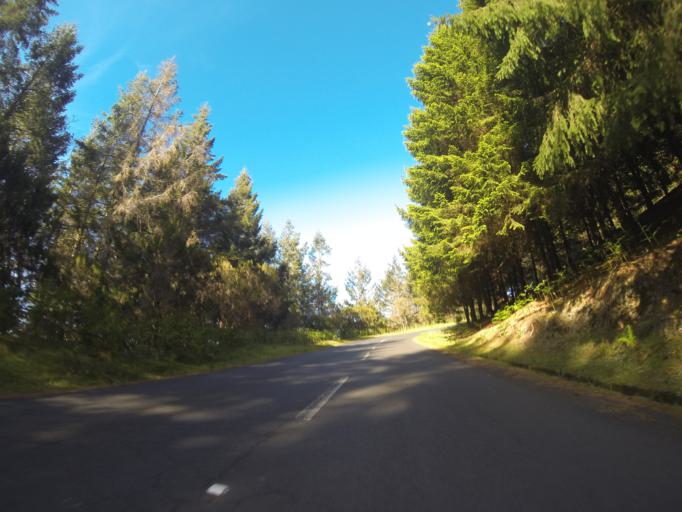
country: PT
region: Madeira
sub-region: Funchal
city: Nossa Senhora do Monte
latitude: 32.7186
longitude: -16.8847
